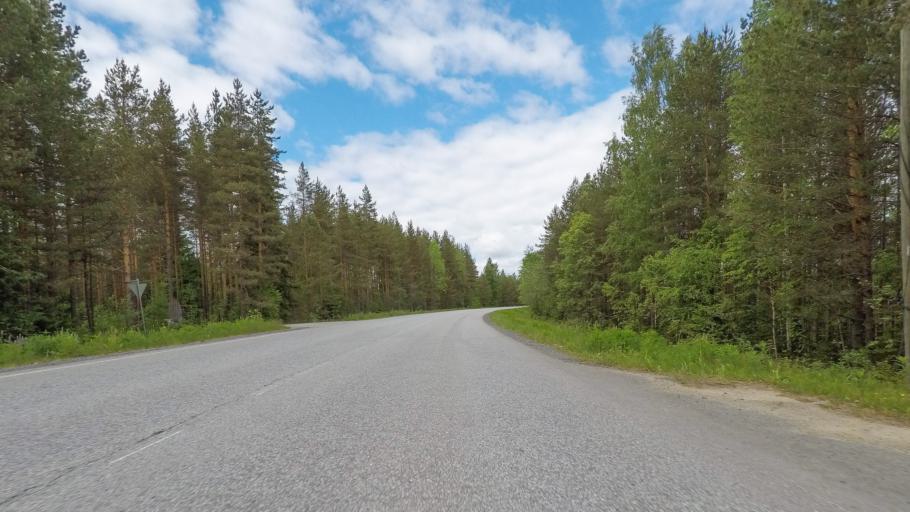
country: FI
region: Central Finland
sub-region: Jyvaeskylae
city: Toivakka
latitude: 62.1281
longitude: 26.1024
